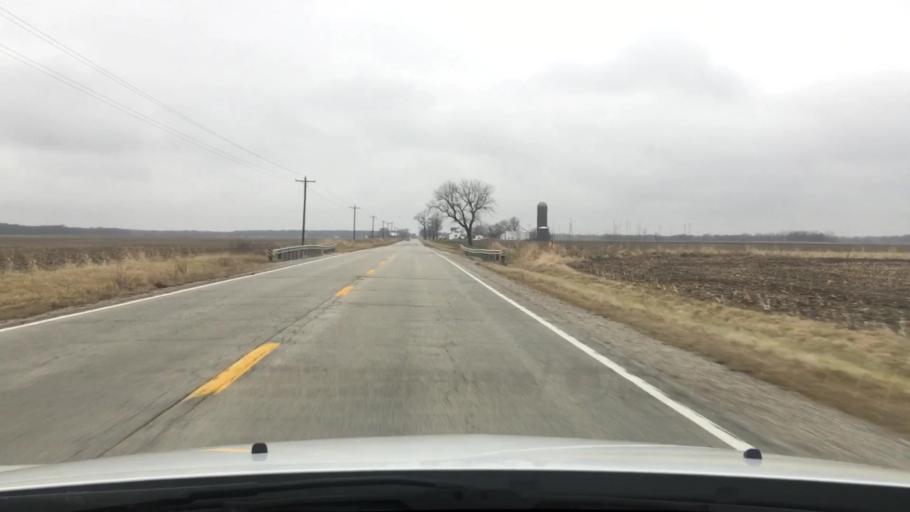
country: US
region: Illinois
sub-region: Iroquois County
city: Watseka
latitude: 40.8886
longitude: -87.7967
